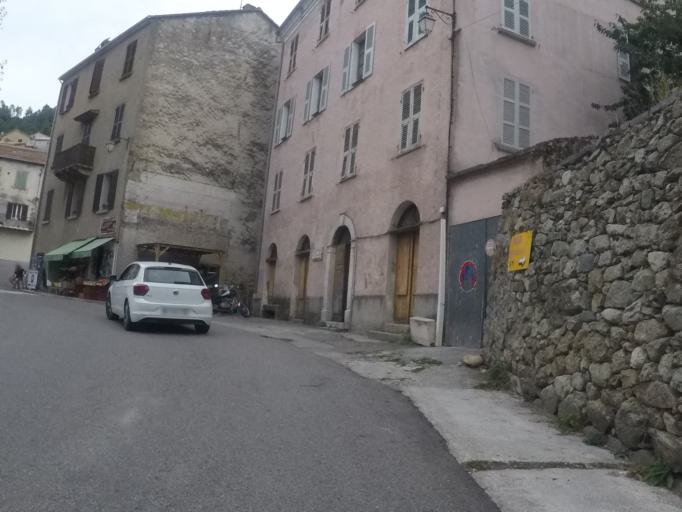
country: FR
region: Corsica
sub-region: Departement de la Haute-Corse
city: Corte
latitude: 42.1728
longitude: 9.1692
